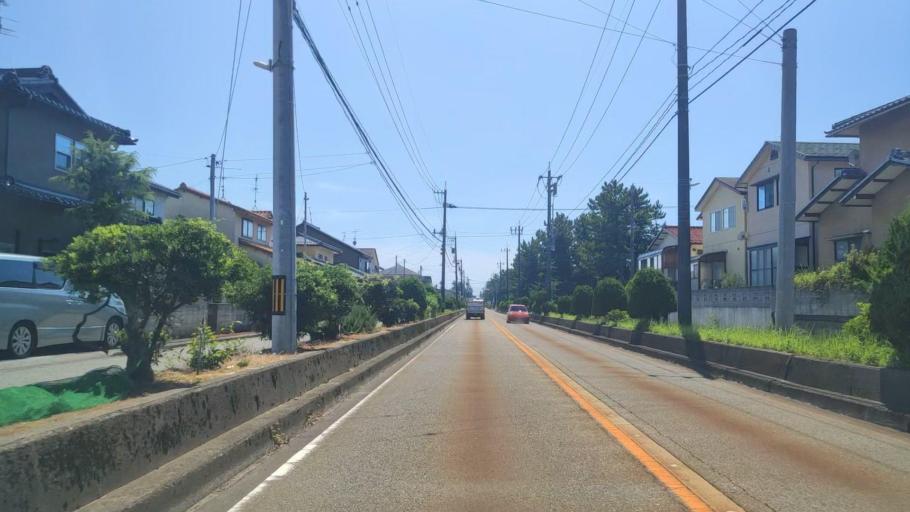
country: JP
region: Ishikawa
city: Kanazawa-shi
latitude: 36.6307
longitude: 136.6255
